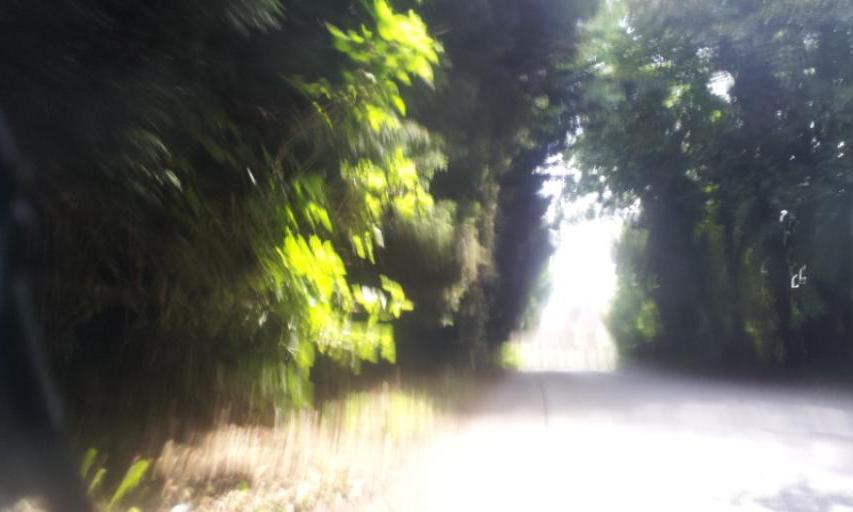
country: GB
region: England
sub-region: Kent
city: Yalding
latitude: 51.2367
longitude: 0.4235
